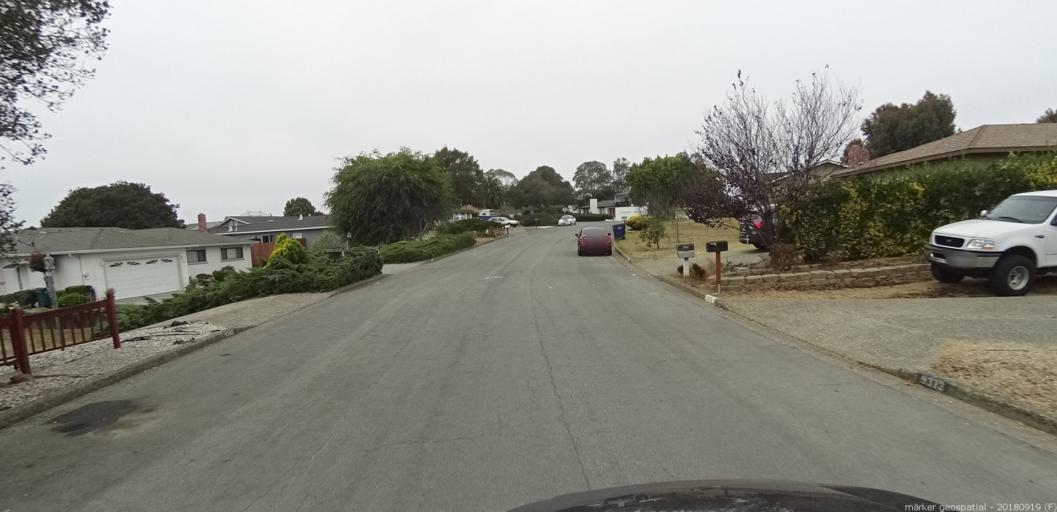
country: US
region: California
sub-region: Monterey County
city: Castroville
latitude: 36.7815
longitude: -121.7155
